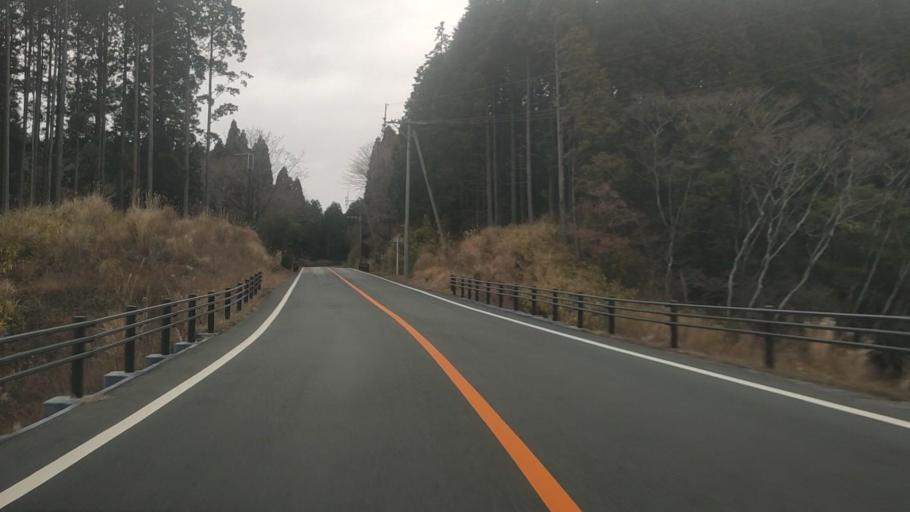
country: JP
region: Kumamoto
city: Aso
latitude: 32.8969
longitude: 131.0281
